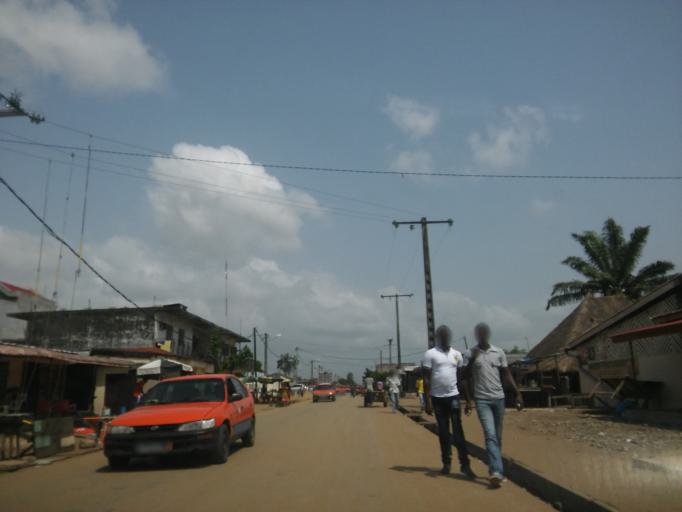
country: CI
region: Sud-Comoe
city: Grand-Bassam
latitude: 5.2119
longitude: -3.7376
